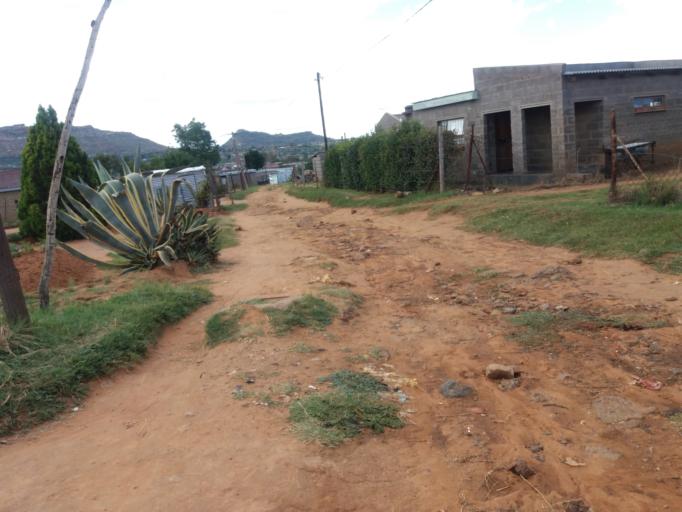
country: LS
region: Maseru
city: Maseru
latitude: -29.3690
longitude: 27.5061
